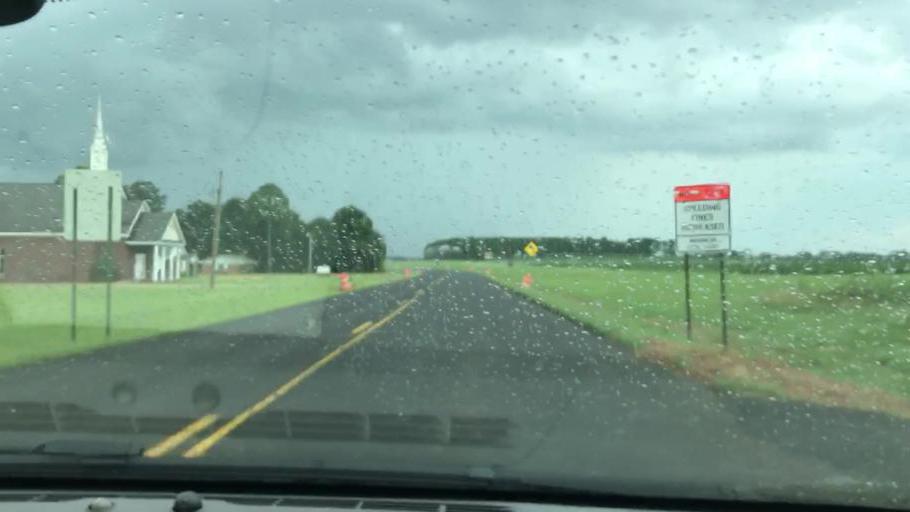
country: US
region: Georgia
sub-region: Clay County
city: Fort Gaines
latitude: 31.4866
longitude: -85.0175
